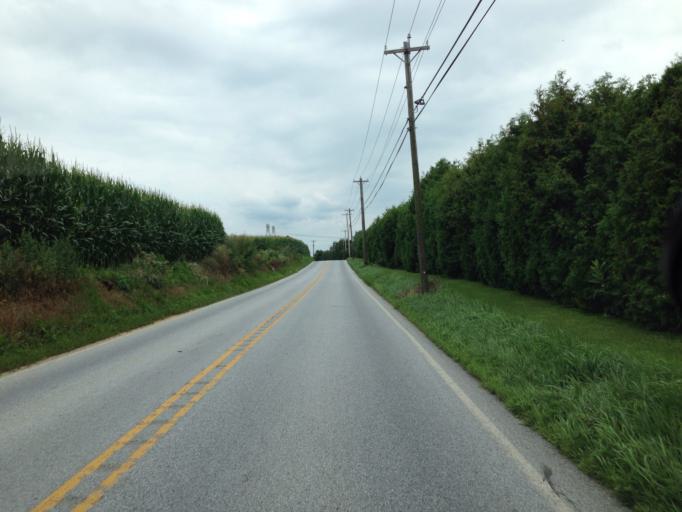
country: US
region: Pennsylvania
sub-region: Chester County
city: Oxford
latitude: 39.8323
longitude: -75.9288
